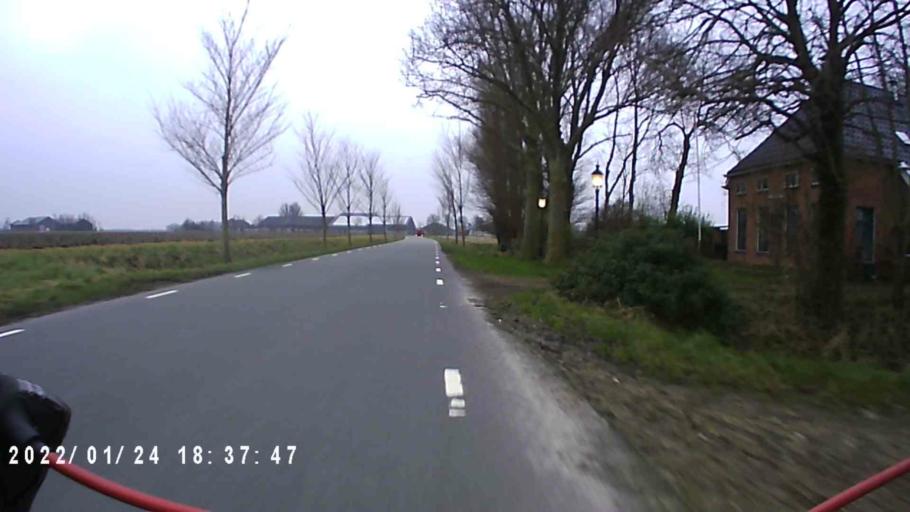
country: NL
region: Groningen
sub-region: Gemeente De Marne
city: Ulrum
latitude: 53.3505
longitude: 6.3360
